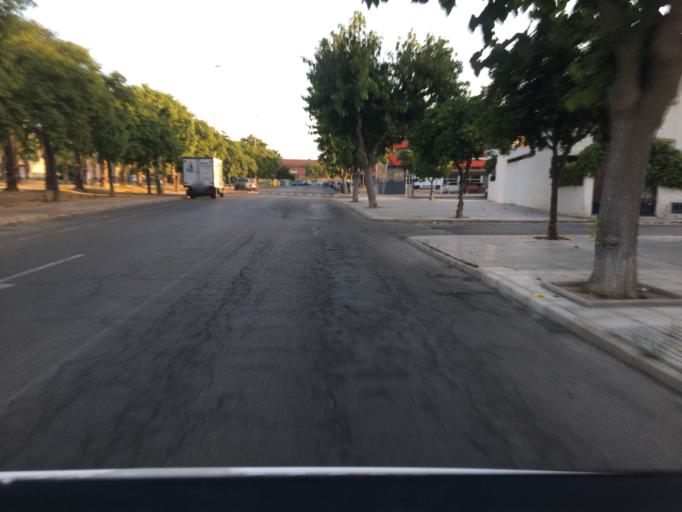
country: ES
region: Murcia
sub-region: Murcia
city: Cartagena
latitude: 37.6207
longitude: -0.9905
